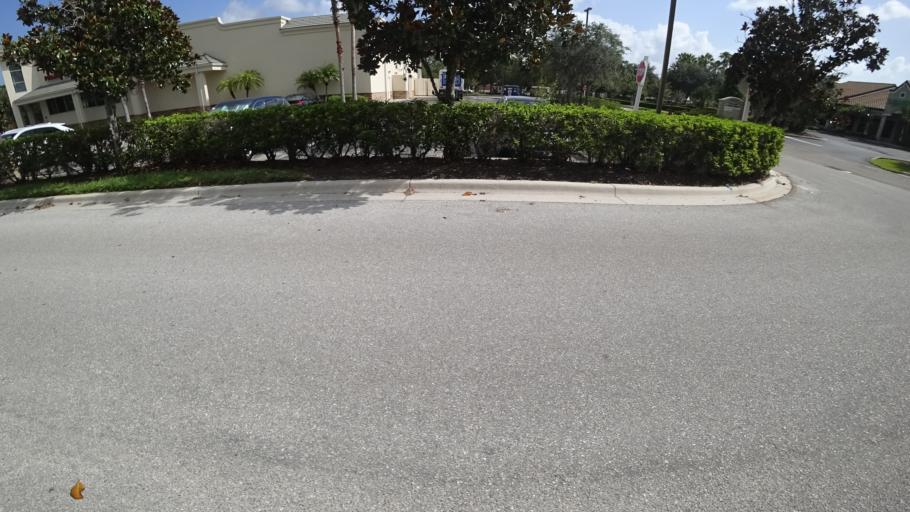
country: US
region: Florida
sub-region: Sarasota County
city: The Meadows
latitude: 27.3903
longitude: -82.4409
